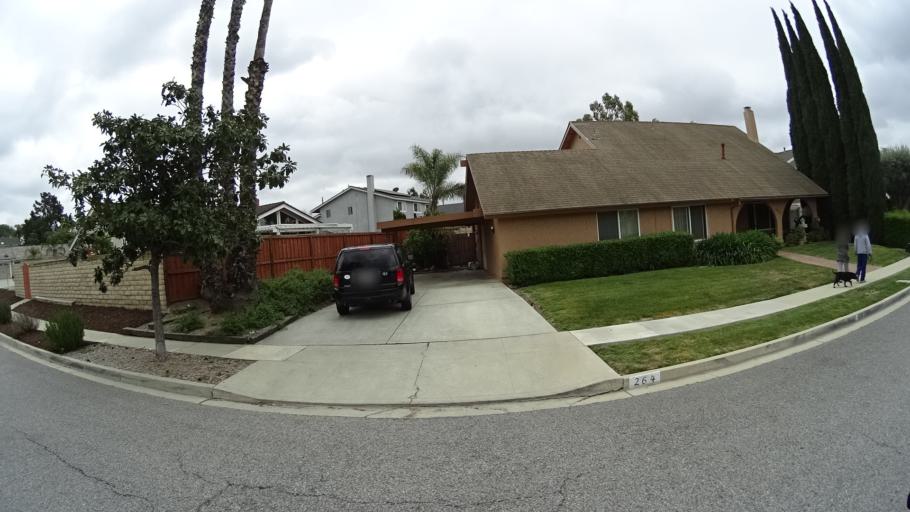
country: US
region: California
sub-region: Ventura County
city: Thousand Oaks
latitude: 34.2169
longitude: -118.8833
